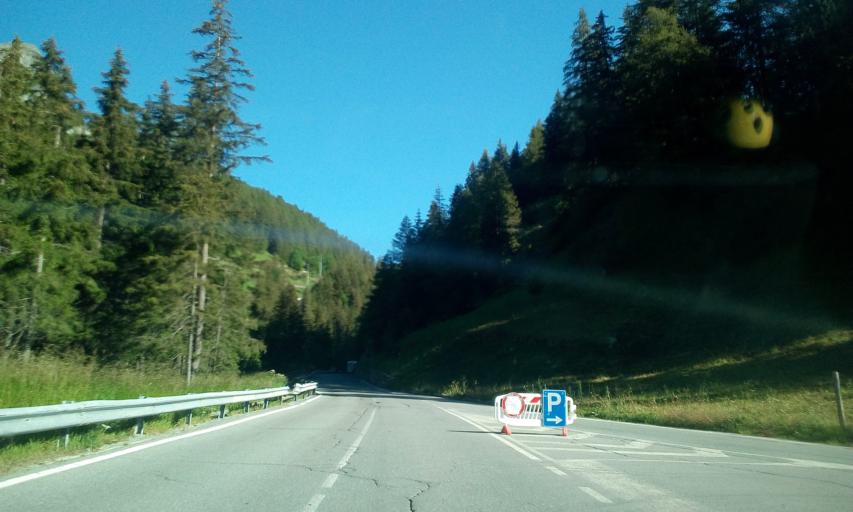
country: IT
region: Aosta Valley
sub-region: Valle d'Aosta
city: Ayas
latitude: 45.8556
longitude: 7.7320
